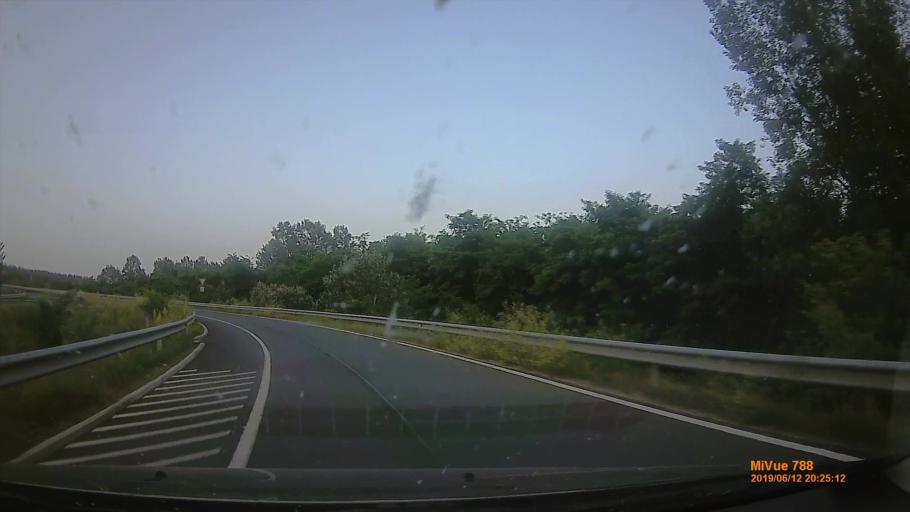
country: HU
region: Pest
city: Gyal
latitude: 47.3664
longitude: 19.2357
